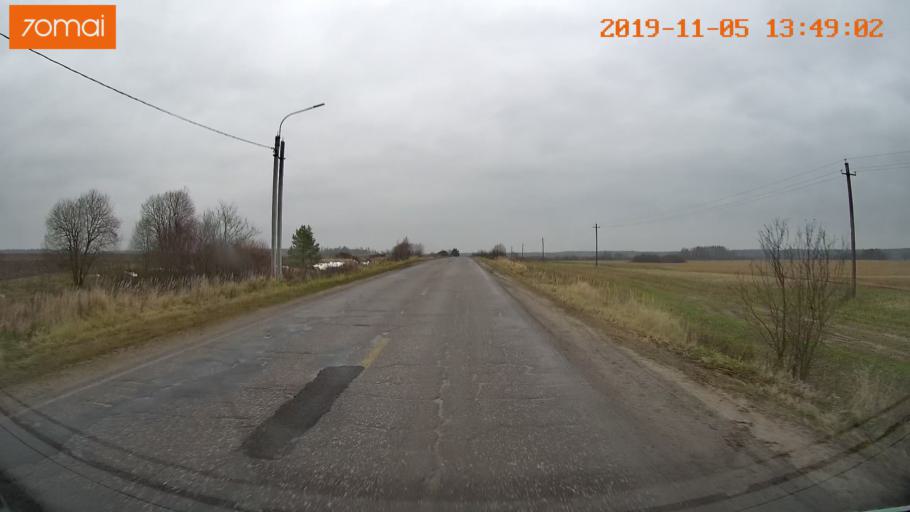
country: RU
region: Ivanovo
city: Kaminskiy
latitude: 57.0069
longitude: 41.4080
